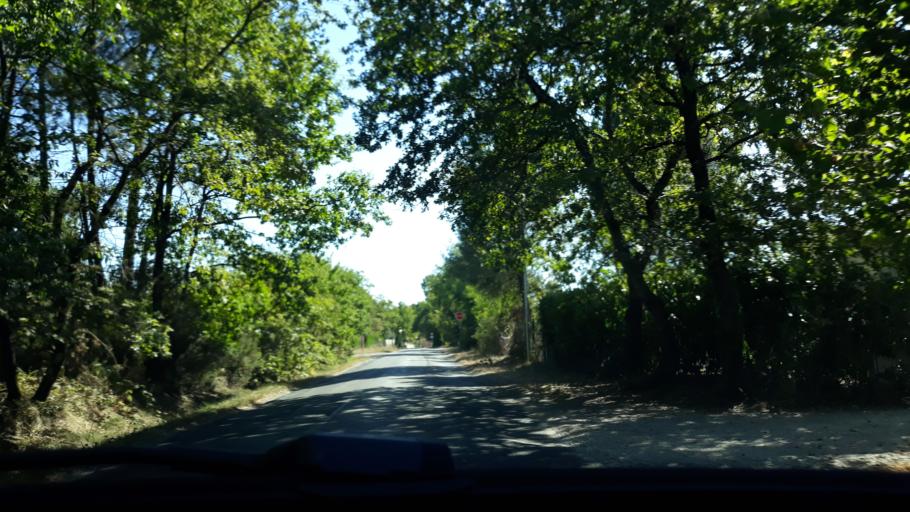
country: FR
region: Aquitaine
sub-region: Departement de la Gironde
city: Leognan
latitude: 44.7397
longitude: -0.6107
